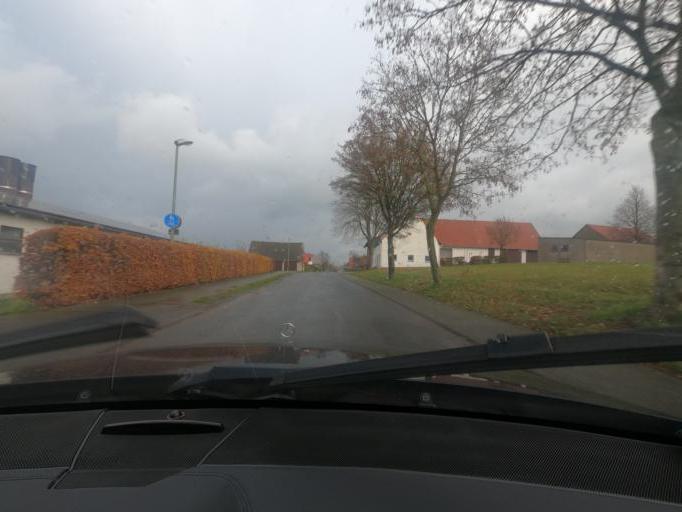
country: DE
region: North Rhine-Westphalia
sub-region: Regierungsbezirk Detmold
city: Wunnenberg
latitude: 51.5709
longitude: 8.7723
